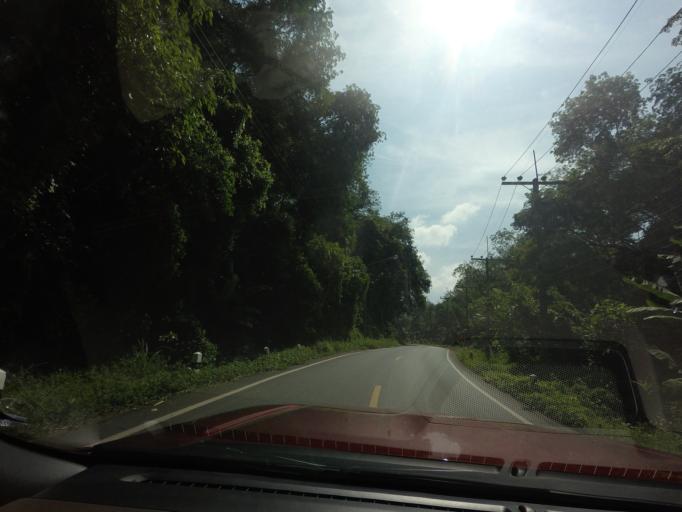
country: TH
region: Yala
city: Betong
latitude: 5.8229
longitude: 101.0755
